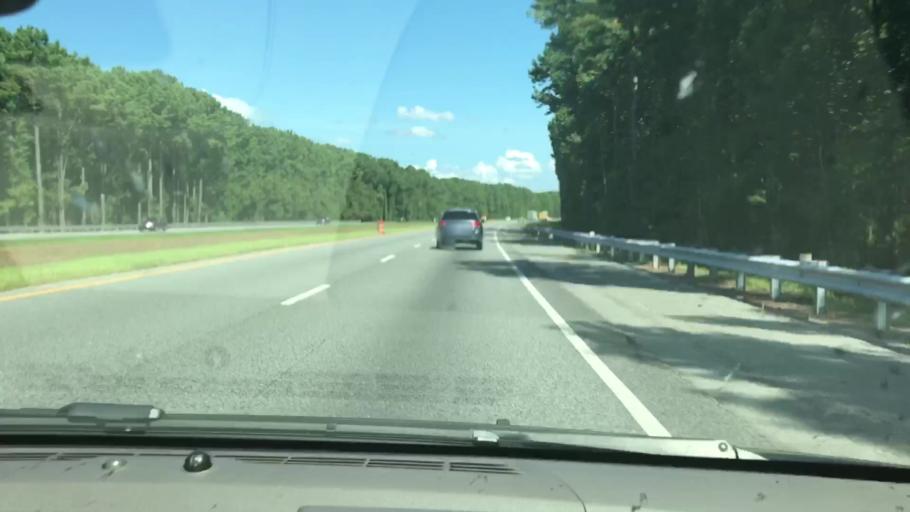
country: US
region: Georgia
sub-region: Harris County
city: Hamilton
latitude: 32.6712
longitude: -84.9869
